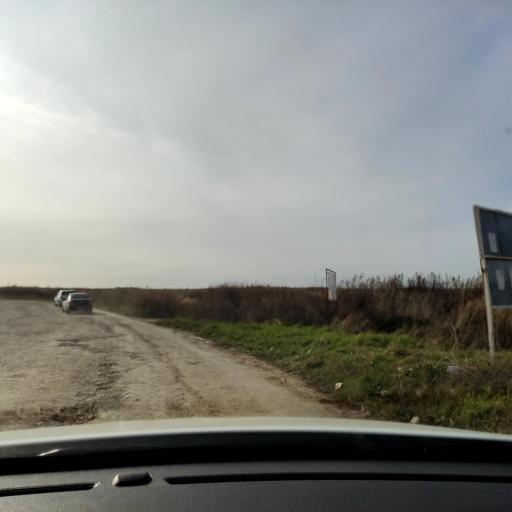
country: RU
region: Tatarstan
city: Vysokaya Gora
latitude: 55.8618
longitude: 49.3618
